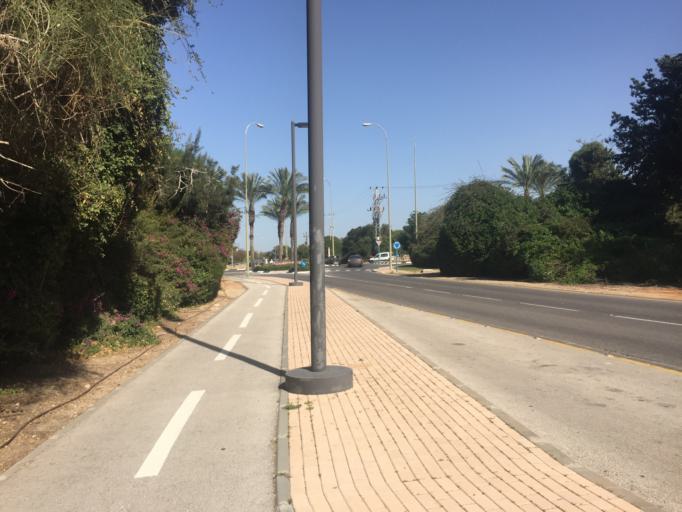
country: IL
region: Haifa
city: Qesarya
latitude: 32.5028
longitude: 34.9039
